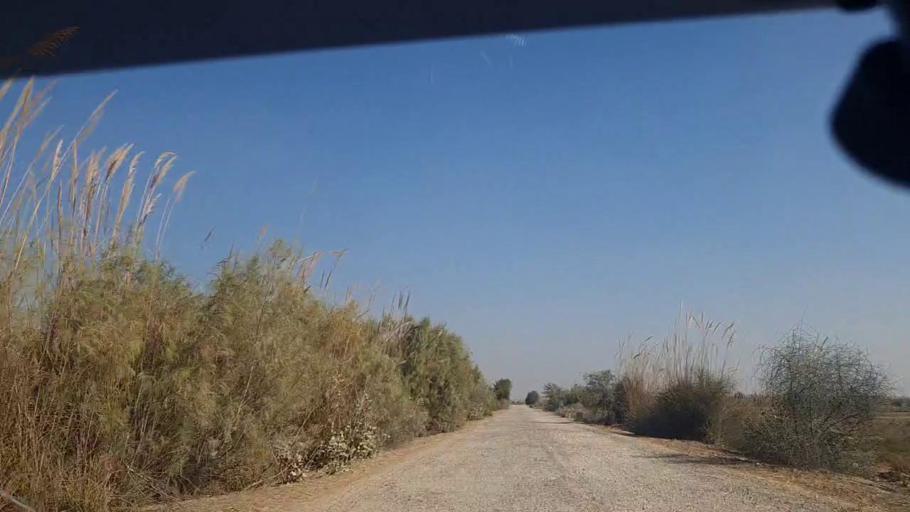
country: PK
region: Sindh
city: Khanpur
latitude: 27.5647
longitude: 69.3061
